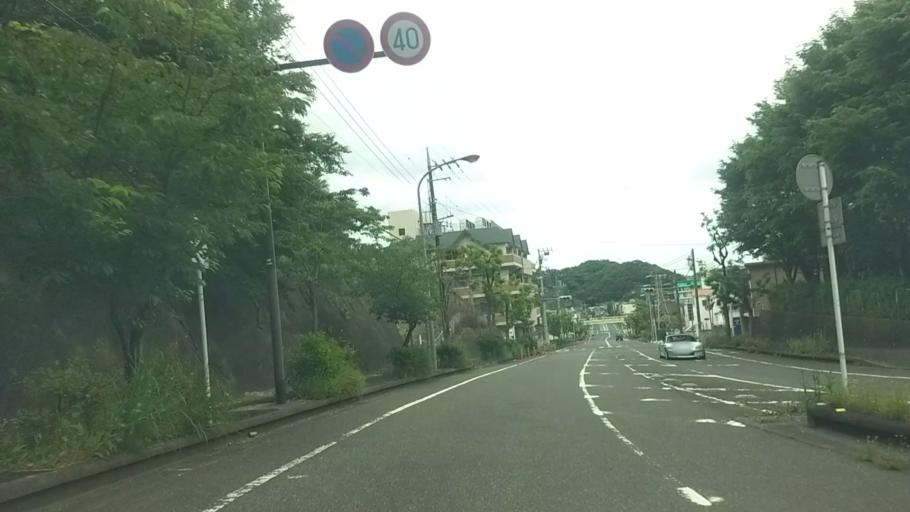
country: JP
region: Kanagawa
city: Fujisawa
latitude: 35.3553
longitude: 139.5170
